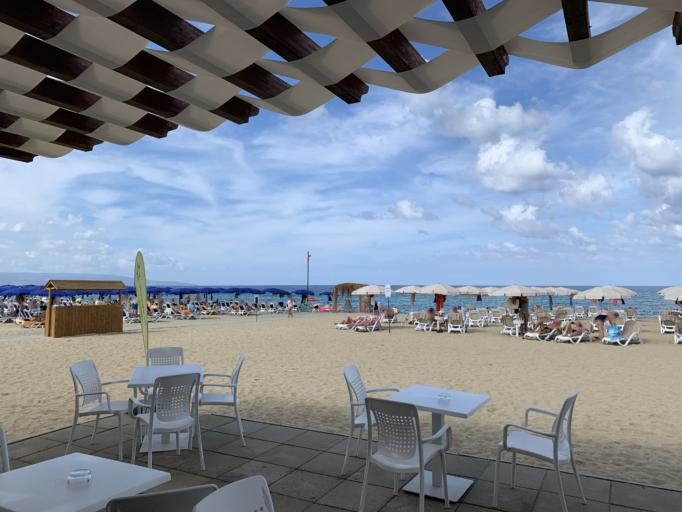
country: IT
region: Calabria
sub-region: Provincia di Vibo-Valentia
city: Pizzo
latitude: 38.8026
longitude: 16.2112
